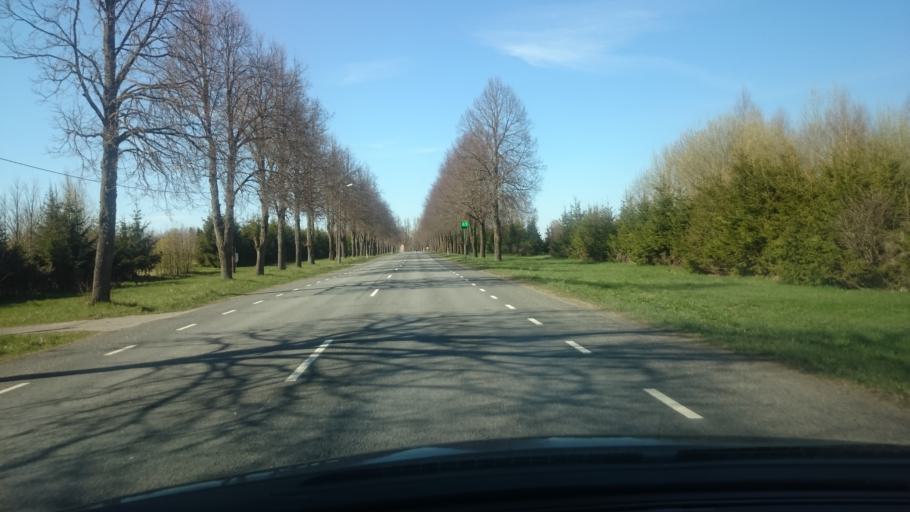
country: EE
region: Polvamaa
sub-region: Polva linn
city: Polva
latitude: 58.2018
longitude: 27.0767
